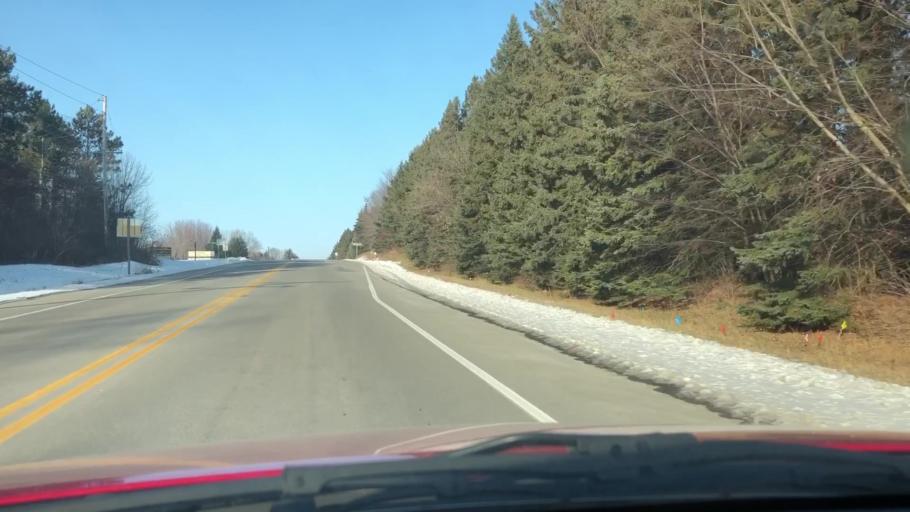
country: US
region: Wisconsin
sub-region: Outagamie County
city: Kimberly
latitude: 44.3278
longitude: -88.3750
